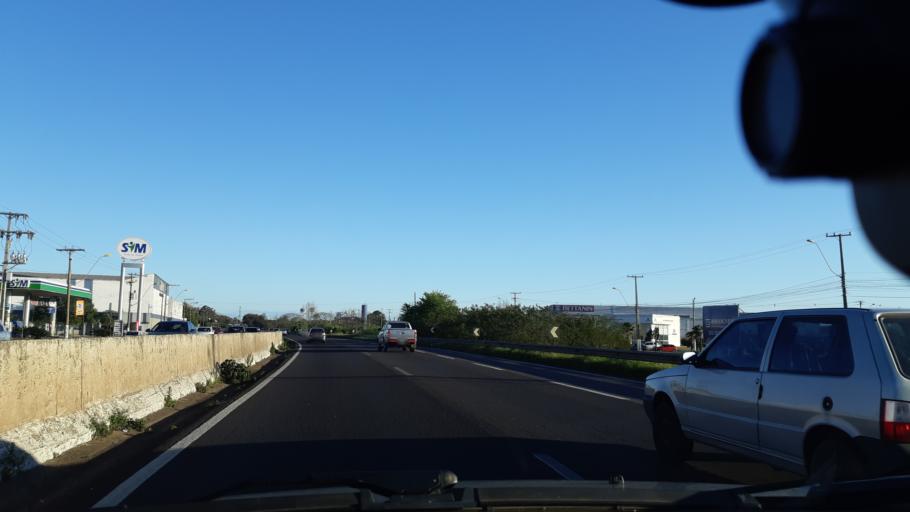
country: BR
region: Rio Grande do Sul
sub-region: Esteio
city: Esteio
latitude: -29.8600
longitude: -51.1810
